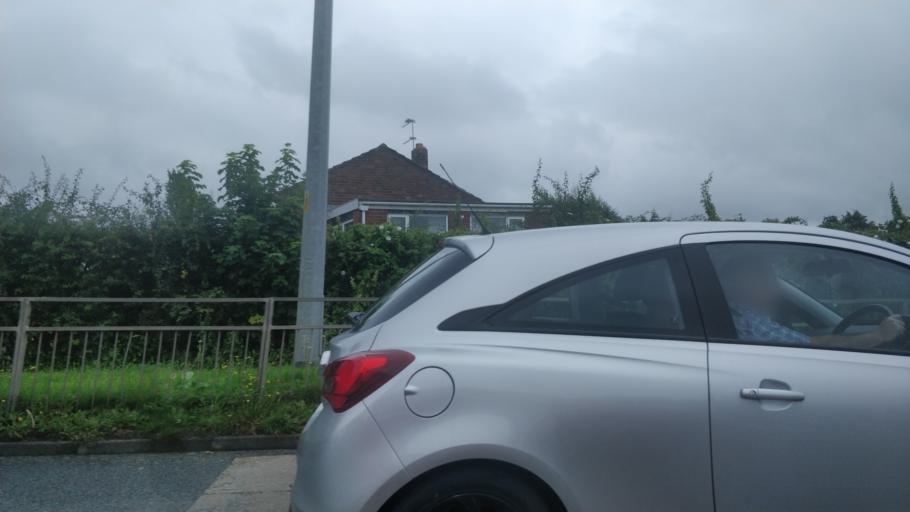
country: GB
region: England
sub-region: Sefton
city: Maghull
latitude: 53.5073
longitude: -2.9440
